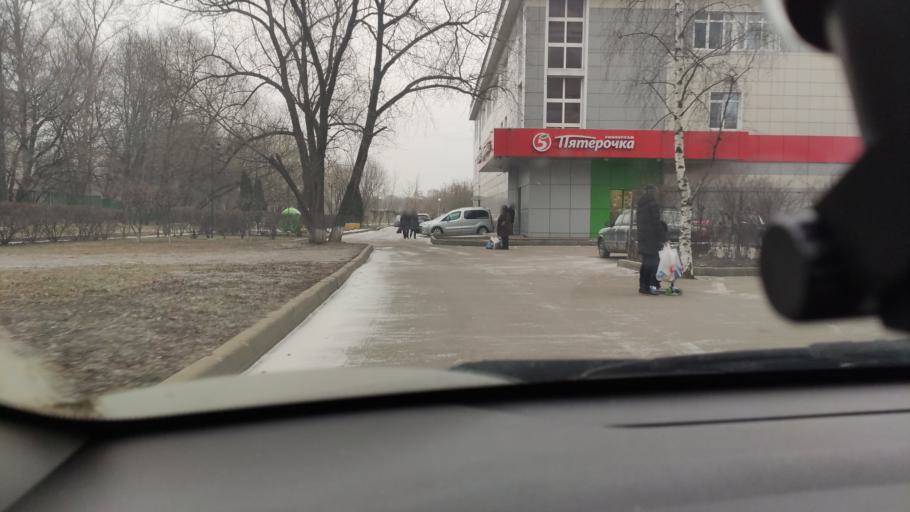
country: RU
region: Moscow
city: Chertanovo Yuzhnoye
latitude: 55.6045
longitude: 37.6158
